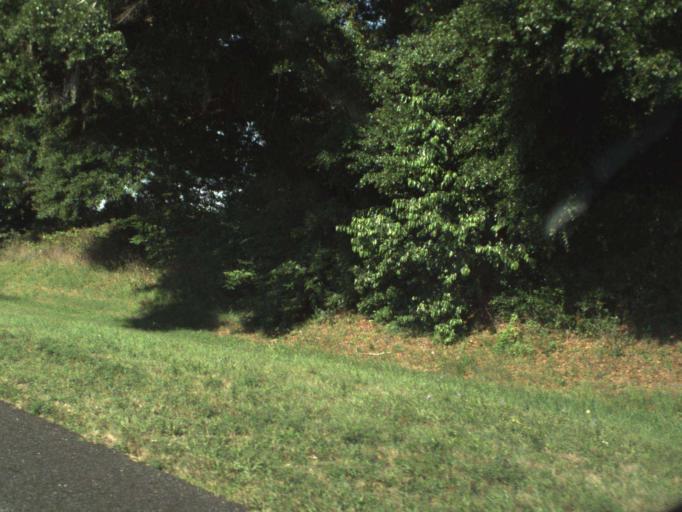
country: US
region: Florida
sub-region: Marion County
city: Citra
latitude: 29.3584
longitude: -82.1409
